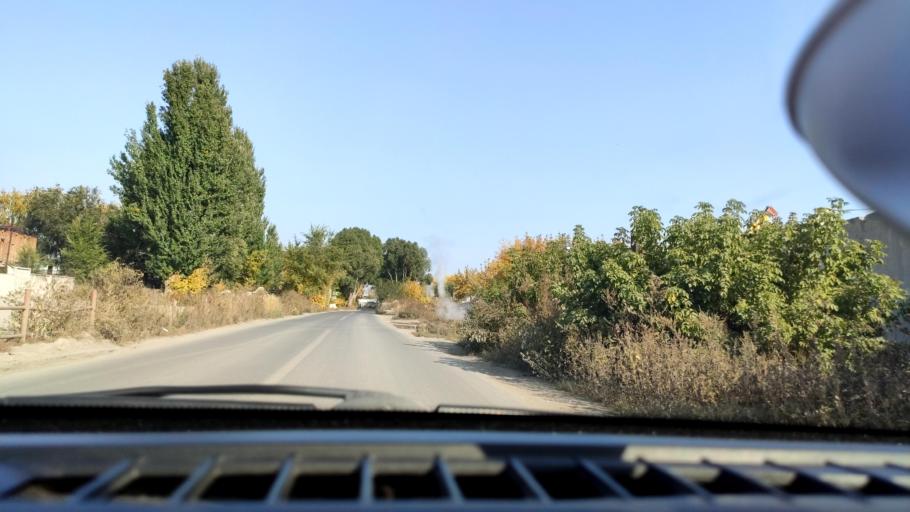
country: RU
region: Samara
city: Samara
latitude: 53.1918
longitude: 50.2699
